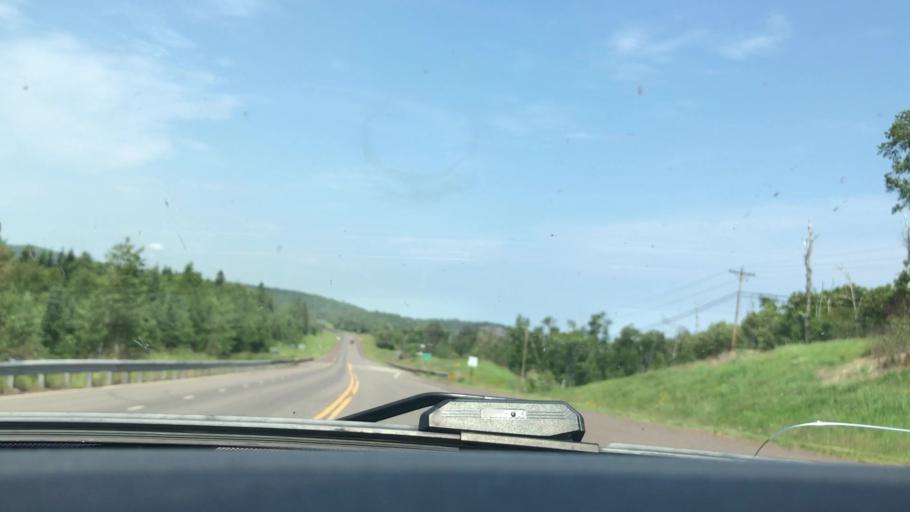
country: US
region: Minnesota
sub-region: Lake County
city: Silver Bay
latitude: 47.3216
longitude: -91.2171
